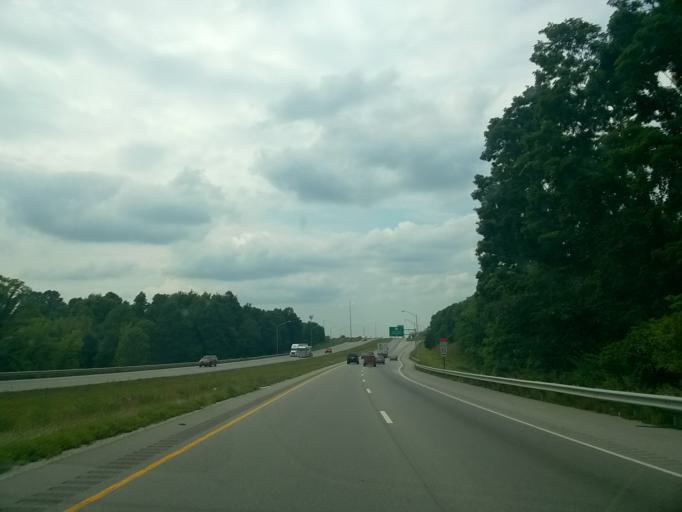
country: US
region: Indiana
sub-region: Putnam County
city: Cloverdale
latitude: 39.5328
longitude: -86.7958
